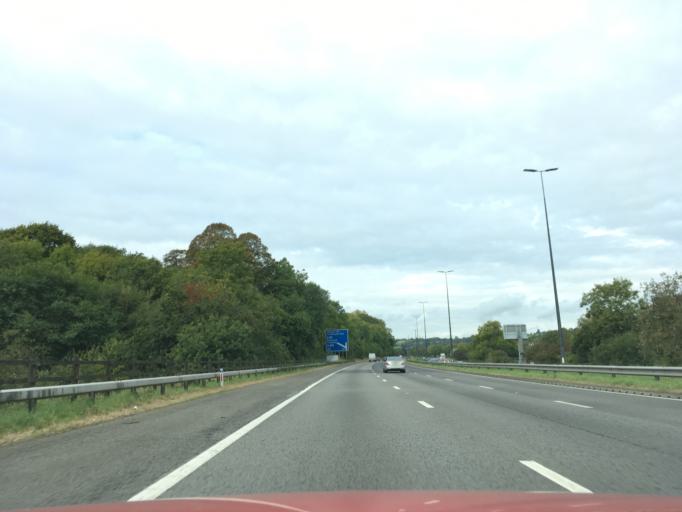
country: GB
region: Wales
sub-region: Newport
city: Langstone
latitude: 51.6005
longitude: -2.8914
